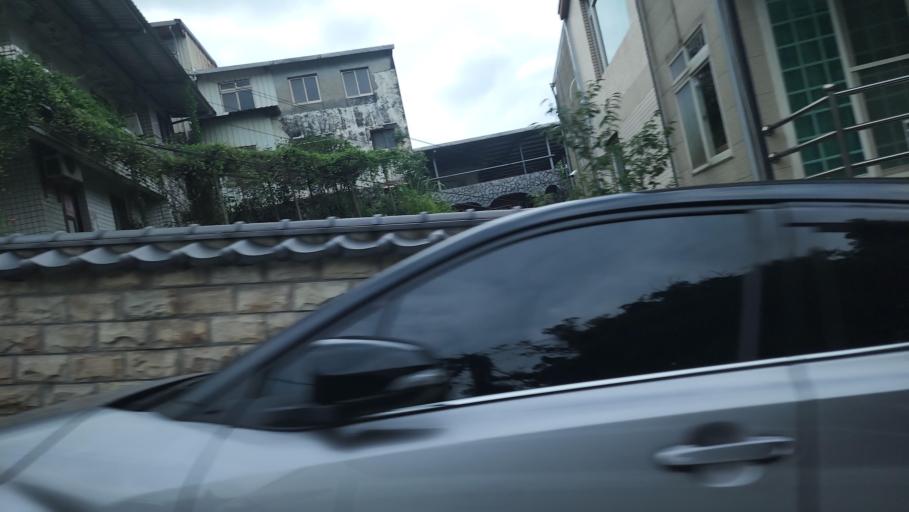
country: TW
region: Taiwan
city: Daxi
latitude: 24.9092
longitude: 121.3906
